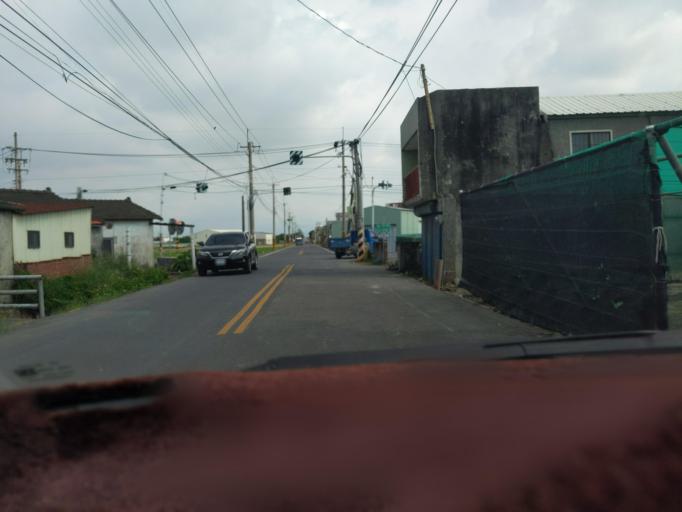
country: TW
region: Taiwan
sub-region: Yunlin
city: Douliu
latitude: 23.7945
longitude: 120.4210
